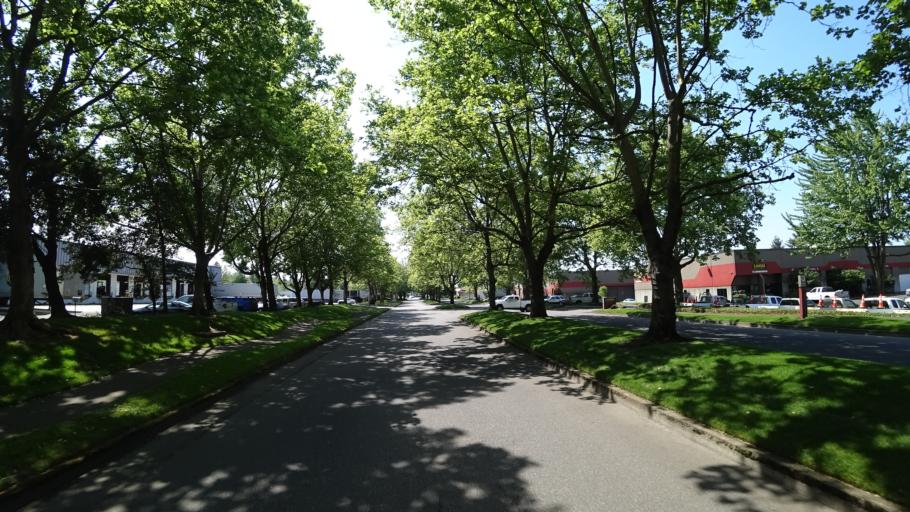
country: US
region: Oregon
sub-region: Multnomah County
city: Lents
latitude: 45.5597
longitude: -122.5404
